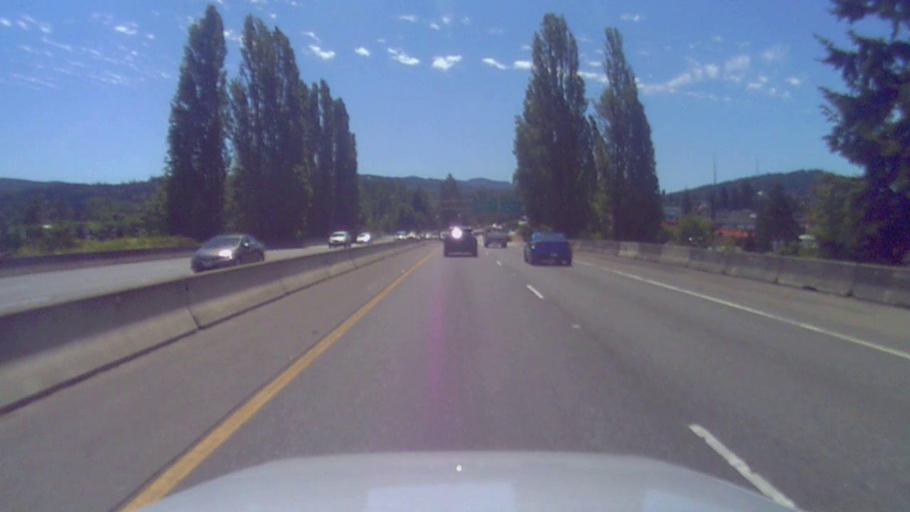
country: US
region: Washington
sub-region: Whatcom County
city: Bellingham
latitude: 48.7569
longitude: -122.4618
